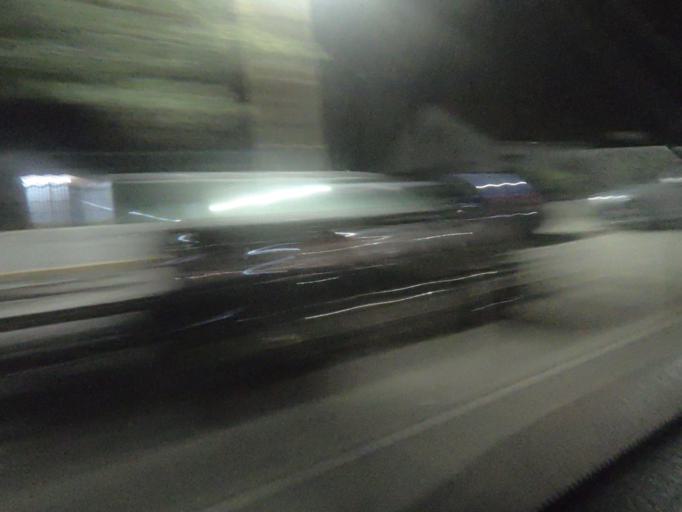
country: PT
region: Setubal
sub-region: Setubal
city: Setubal
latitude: 38.5209
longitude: -8.8264
